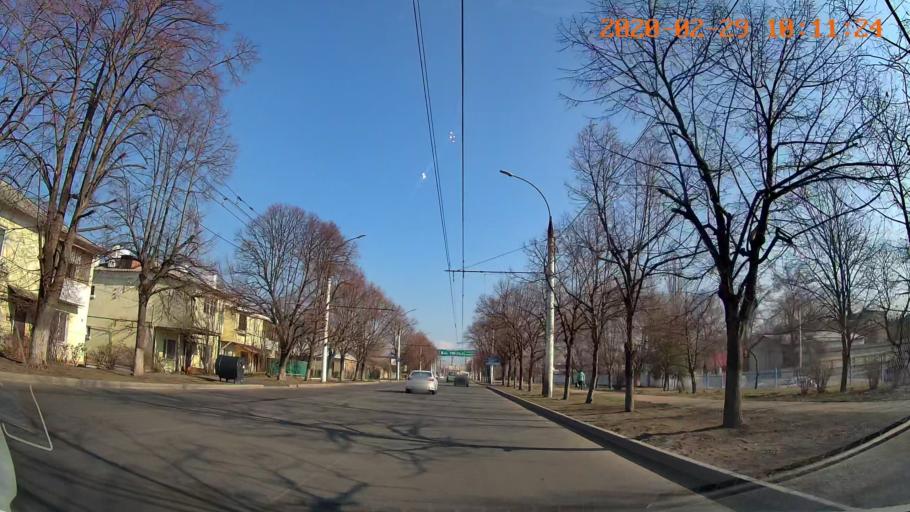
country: MD
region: Telenesti
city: Tiraspolul Nou
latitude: 46.8351
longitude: 29.6439
